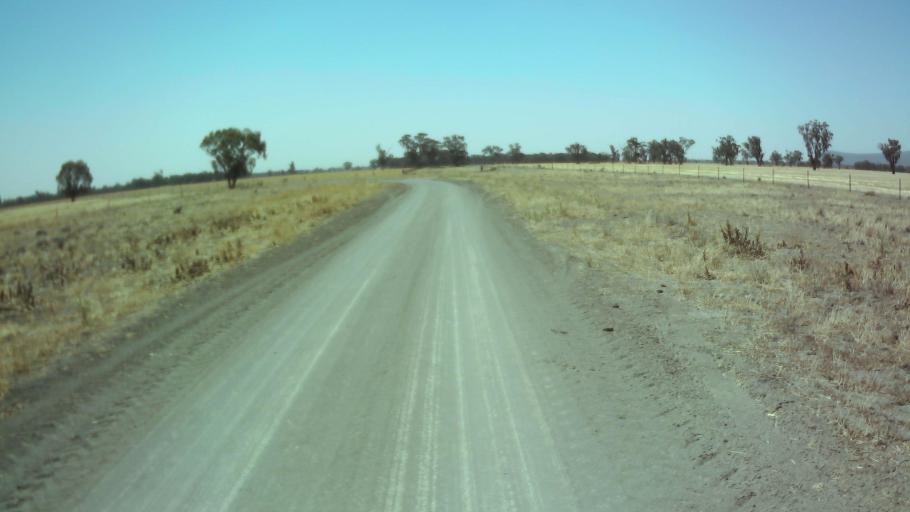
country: AU
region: New South Wales
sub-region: Weddin
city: Grenfell
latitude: -33.9936
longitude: 147.8651
